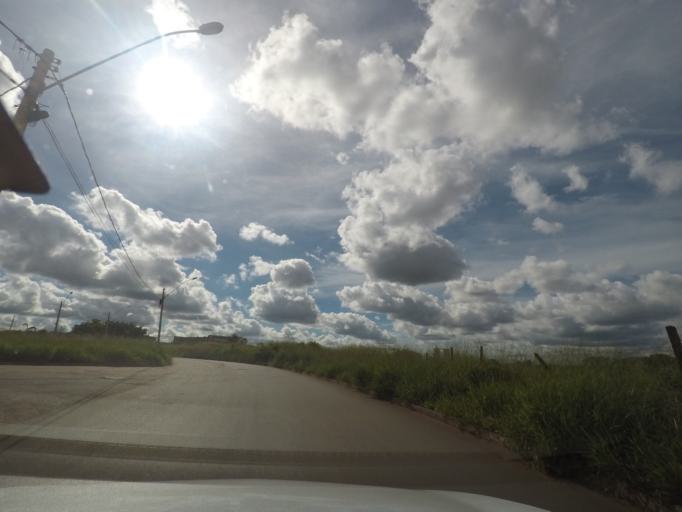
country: BR
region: Goias
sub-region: Goiania
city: Goiania
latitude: -16.7163
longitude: -49.3579
